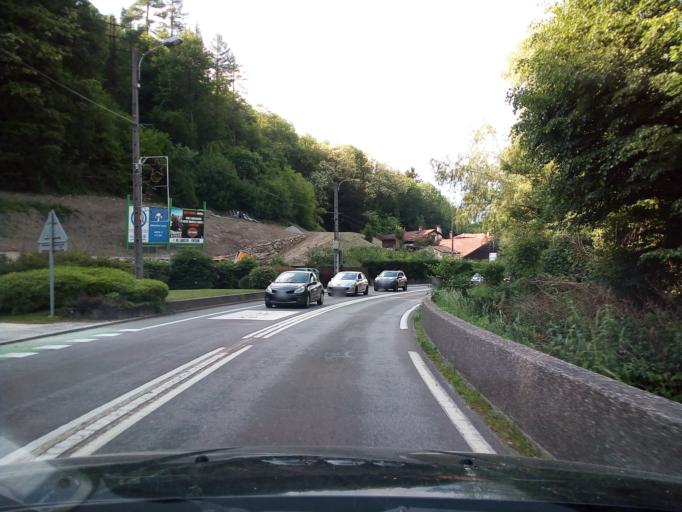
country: FR
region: Rhone-Alpes
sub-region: Departement de l'Isere
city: Gieres
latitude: 45.1759
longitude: 5.7897
